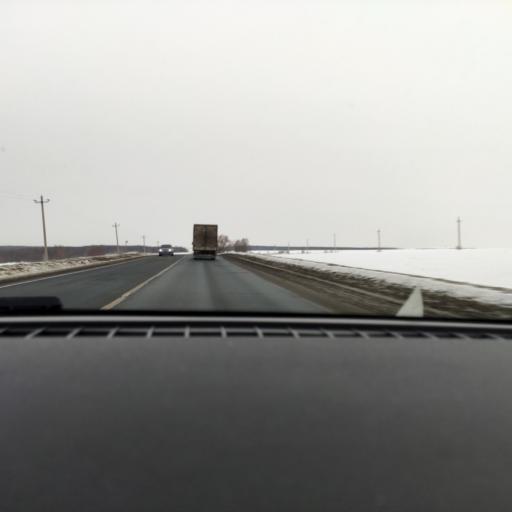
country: RU
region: Samara
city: Petra-Dubrava
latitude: 53.3107
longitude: 50.4571
